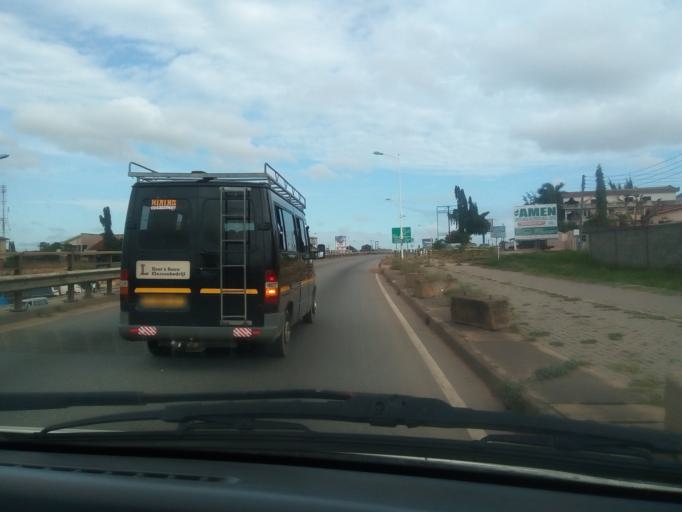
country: GH
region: Greater Accra
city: Dome
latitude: 5.6468
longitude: -0.2488
